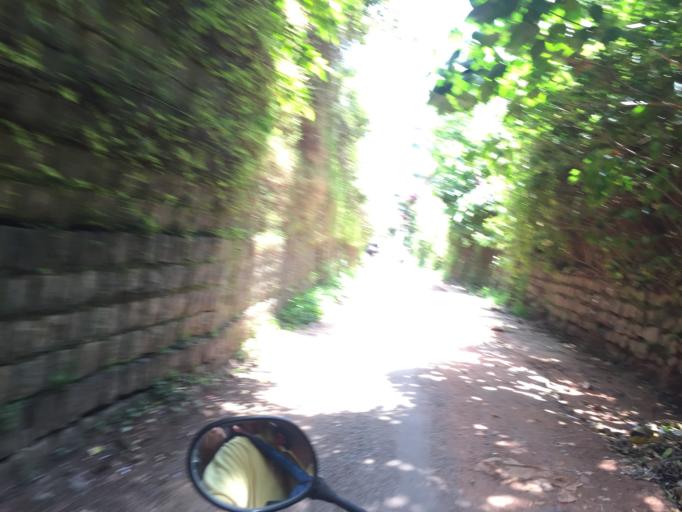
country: IN
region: Karnataka
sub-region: Dakshina Kannada
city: Mangalore
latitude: 12.8745
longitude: 74.8419
